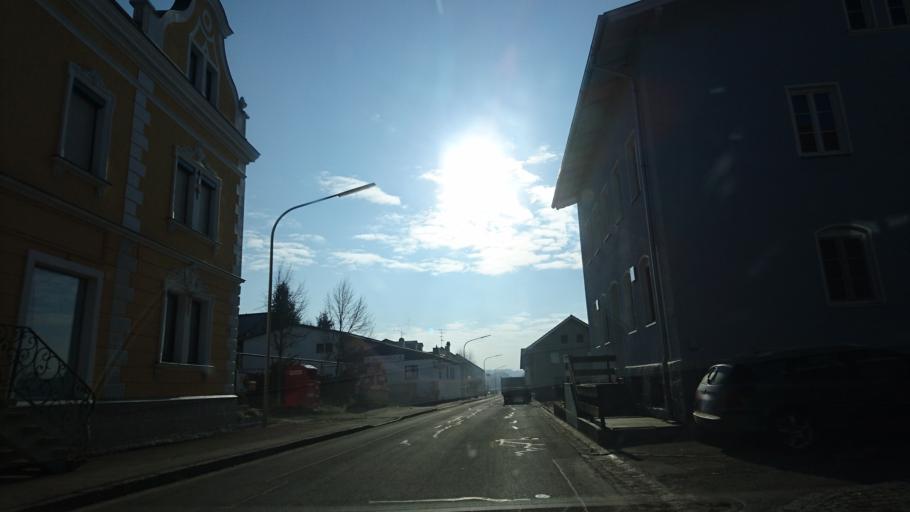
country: DE
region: Bavaria
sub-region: Lower Bavaria
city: Bad Griesbach
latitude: 48.4186
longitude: 13.2145
